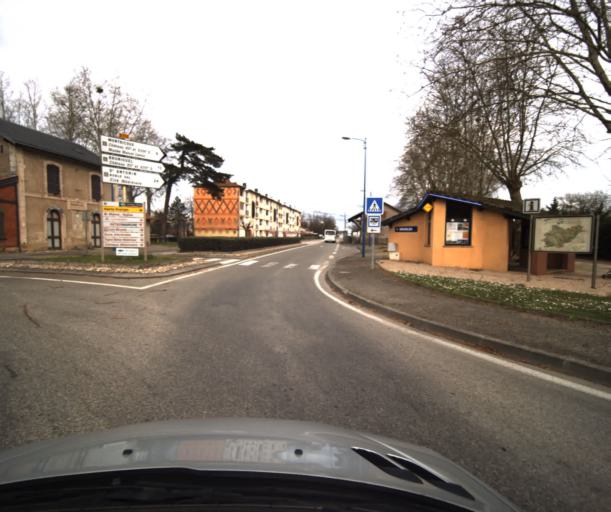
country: FR
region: Midi-Pyrenees
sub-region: Departement du Tarn-et-Garonne
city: Negrepelisse
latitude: 44.0718
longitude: 1.5235
